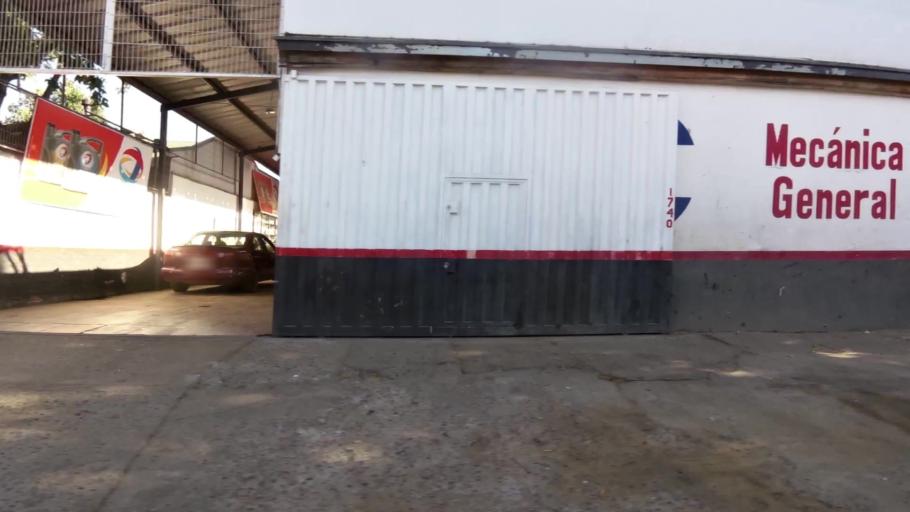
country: CL
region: Maule
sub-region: Provincia de Talca
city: Talca
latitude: -35.4177
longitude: -71.6497
